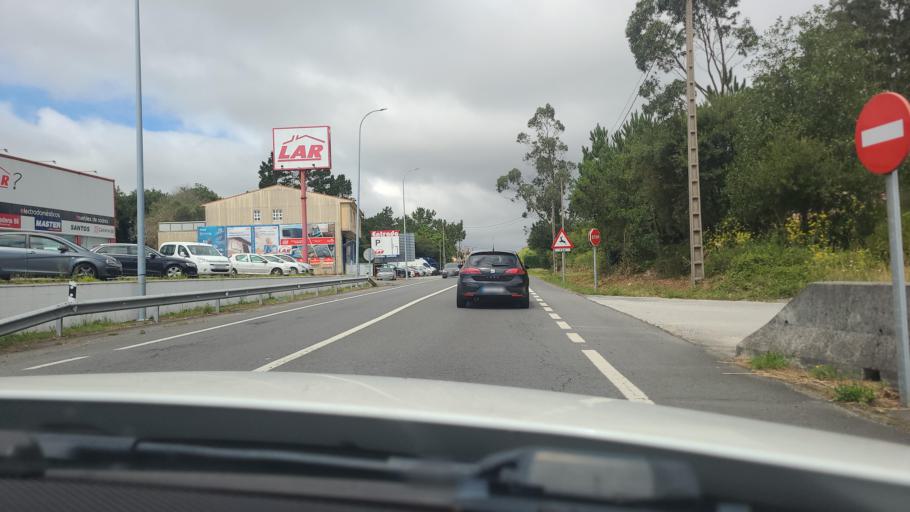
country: ES
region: Galicia
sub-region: Provincia da Coruna
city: Cee
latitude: 42.9782
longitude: -9.1883
